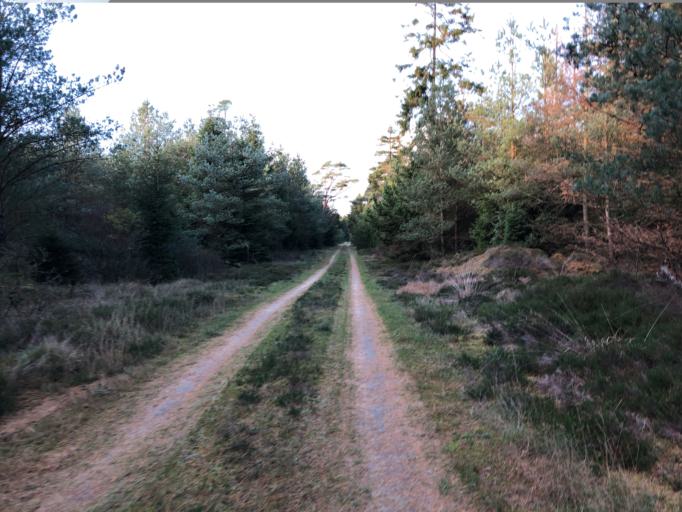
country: DK
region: Central Jutland
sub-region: Holstebro Kommune
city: Ulfborg
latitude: 56.2656
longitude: 8.3831
